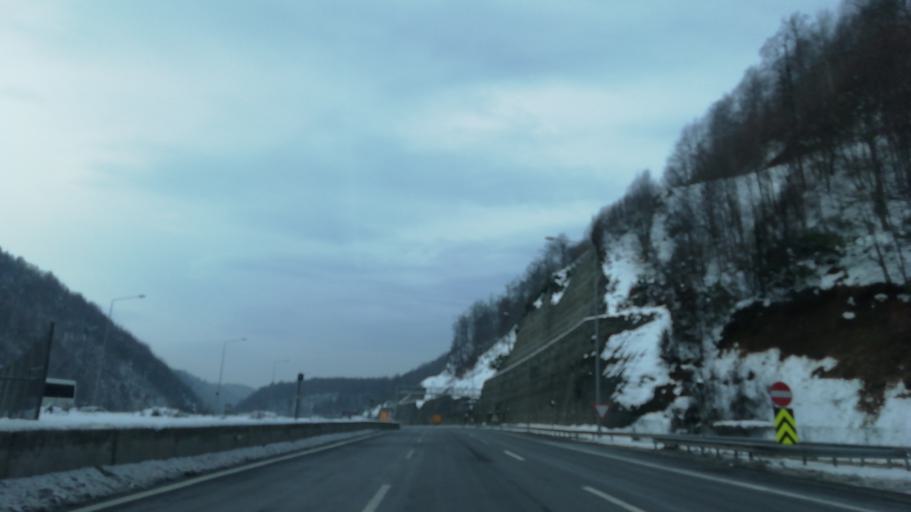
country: TR
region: Duzce
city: Kaynasli
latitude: 40.7583
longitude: 31.4491
